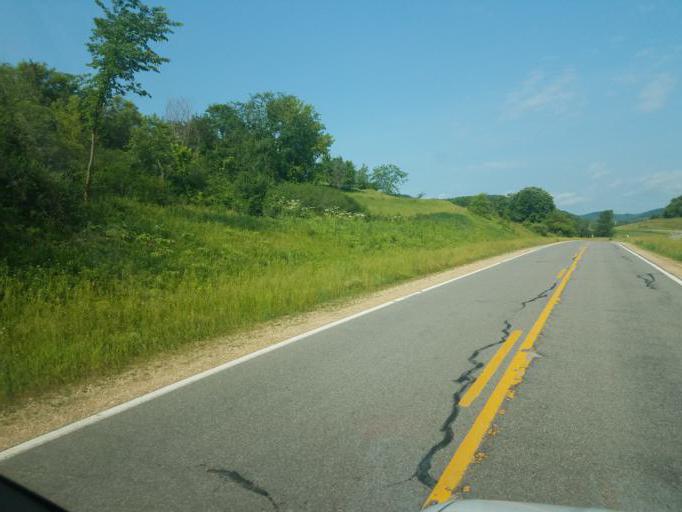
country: US
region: Wisconsin
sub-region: Vernon County
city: Hillsboro
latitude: 43.6787
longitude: -90.5165
